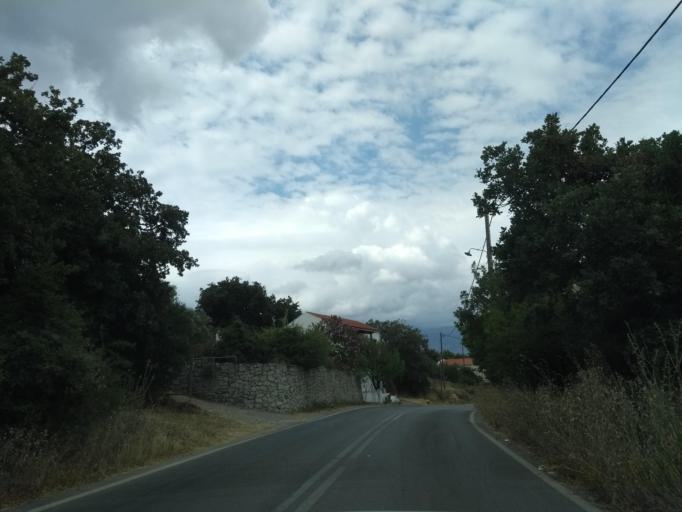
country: GR
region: Crete
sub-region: Nomos Chanias
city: Kalivai
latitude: 35.4082
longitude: 24.2063
